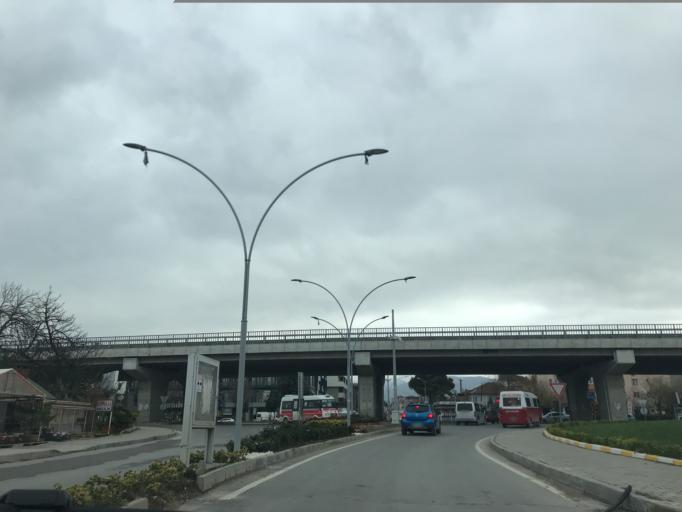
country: TR
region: Yalova
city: Ciftlikkoy
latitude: 40.6650
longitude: 29.3227
